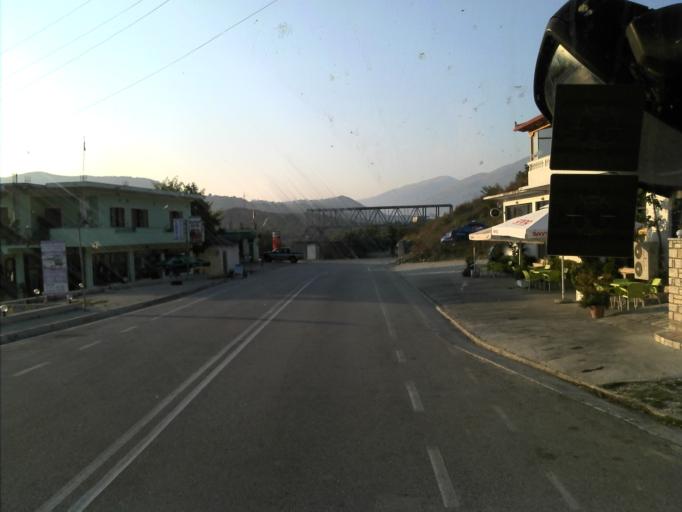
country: AL
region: Gjirokaster
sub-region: Rrethi i Tepelenes
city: Krahes
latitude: 40.4315
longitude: 19.8525
